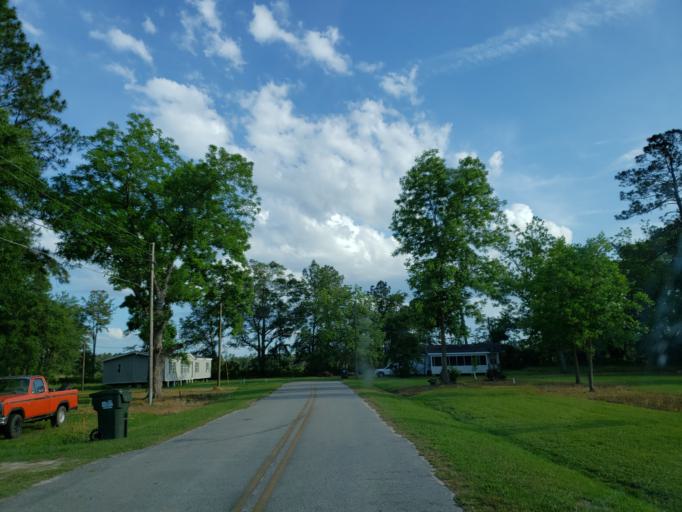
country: US
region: Georgia
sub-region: Lowndes County
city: Hahira
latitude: 31.0436
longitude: -83.3874
